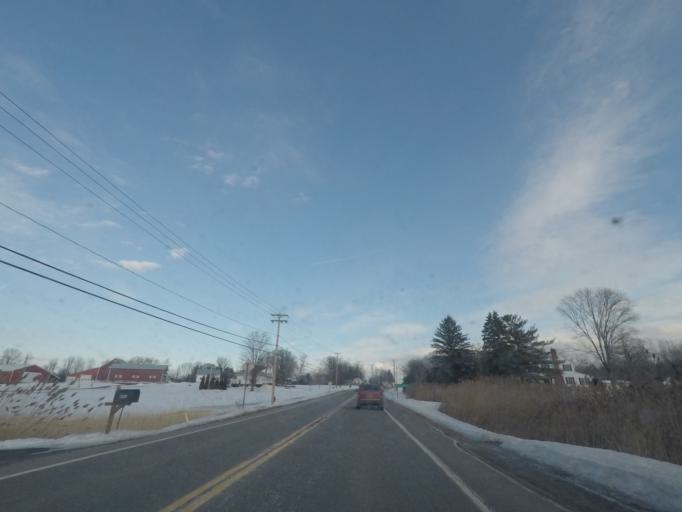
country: US
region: New York
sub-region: Schenectady County
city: Niskayuna
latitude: 42.8350
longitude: -73.8483
